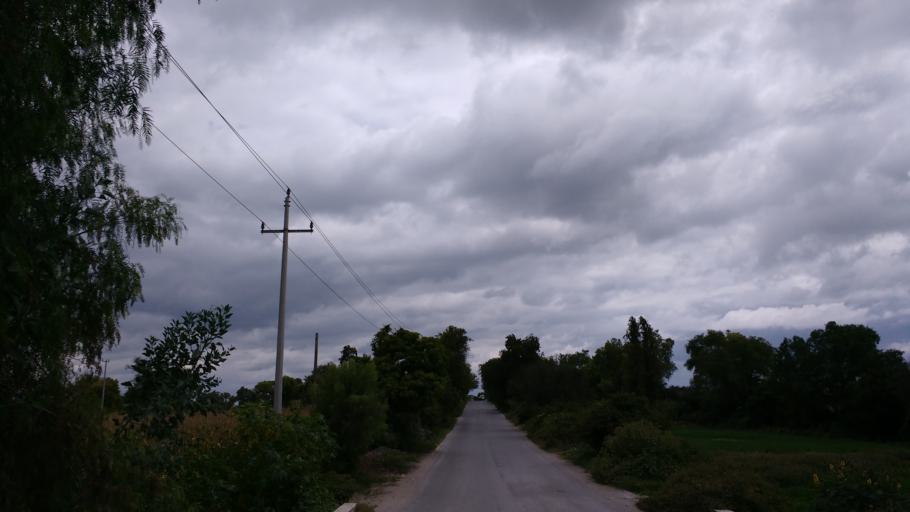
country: MX
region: Hidalgo
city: Mixquiahuala de Juarez
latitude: 20.2459
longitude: -99.2445
